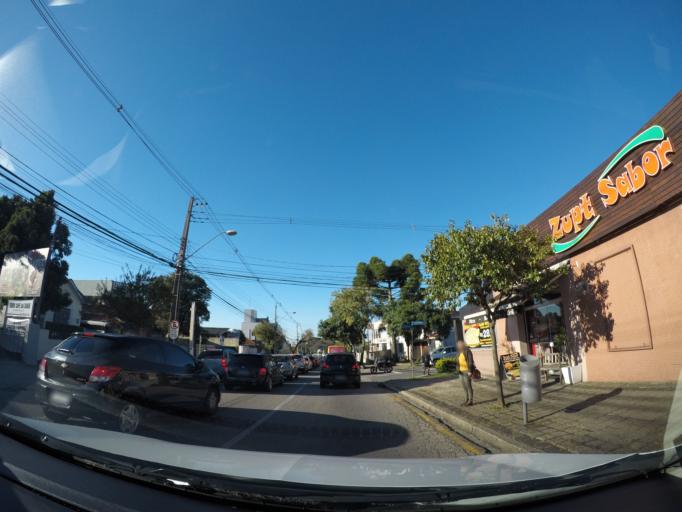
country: BR
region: Parana
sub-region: Curitiba
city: Curitiba
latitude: -25.4086
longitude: -49.2762
